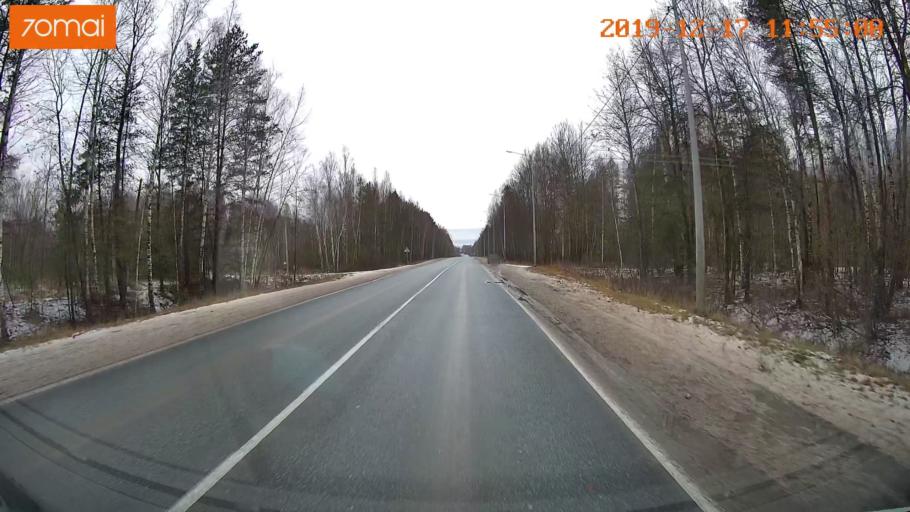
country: RU
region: Rjazan
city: Tuma
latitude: 55.1636
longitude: 40.5606
